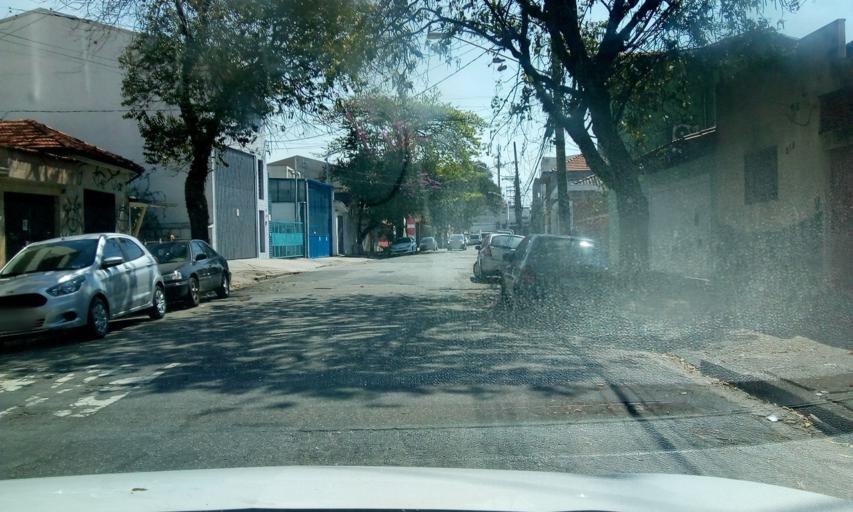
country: BR
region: Sao Paulo
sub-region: Osasco
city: Osasco
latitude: -23.5165
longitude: -46.7211
